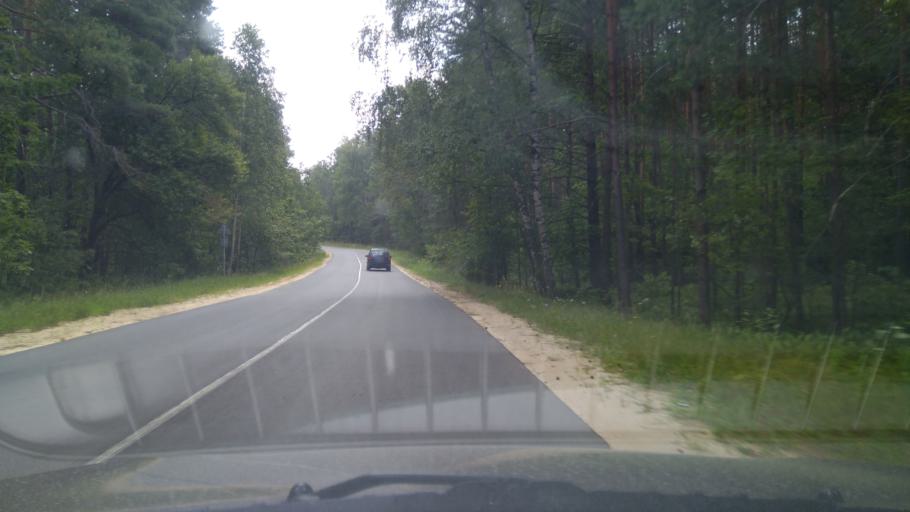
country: BY
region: Brest
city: Nyakhachava
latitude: 52.6028
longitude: 25.0880
